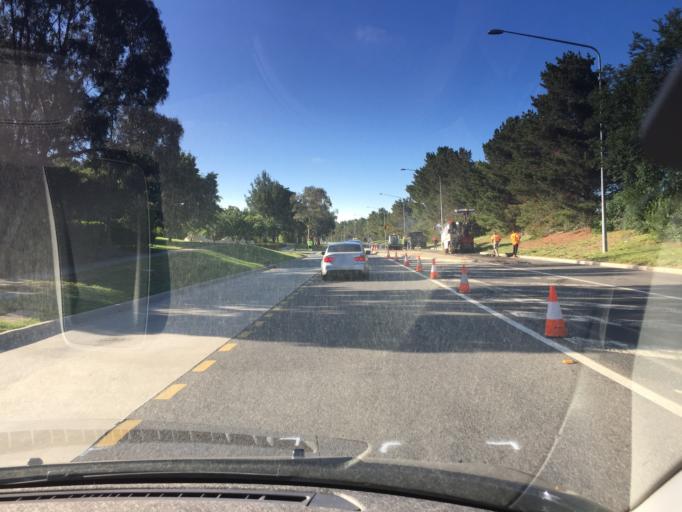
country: AU
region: Australian Capital Territory
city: Kaleen
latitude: -35.2376
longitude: 149.1254
